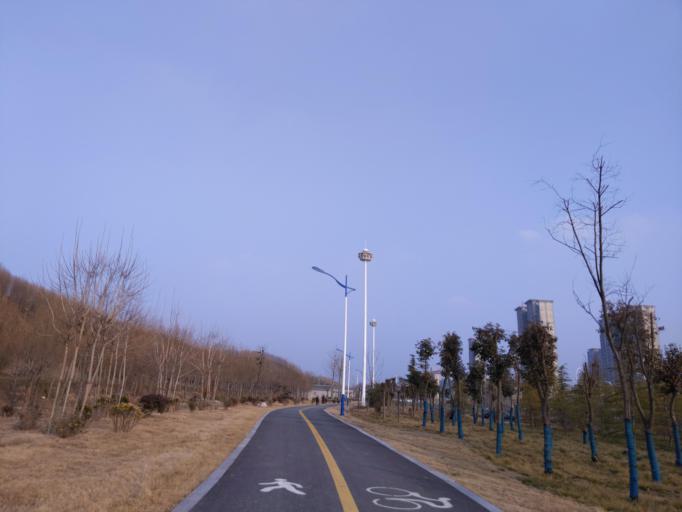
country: CN
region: Henan Sheng
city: Puyang
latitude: 35.8189
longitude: 115.0039
